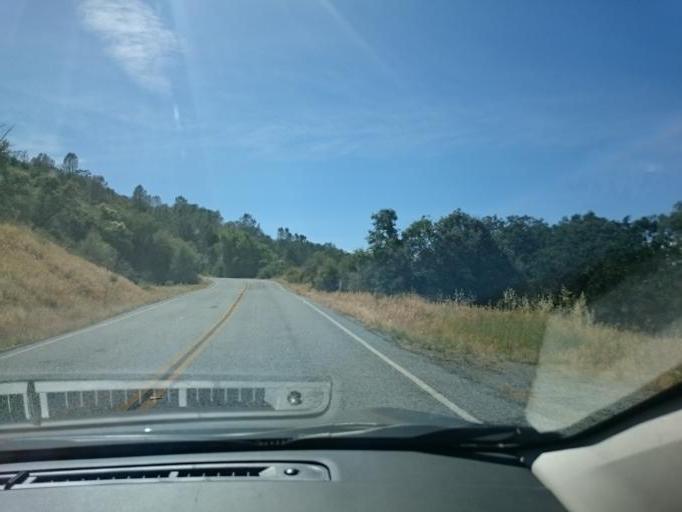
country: US
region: California
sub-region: Santa Clara County
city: Morgan Hill
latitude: 37.3569
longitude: -121.5772
